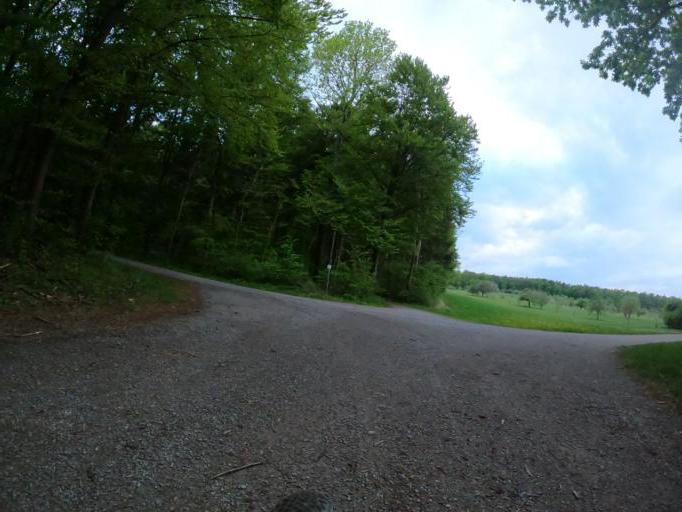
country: DE
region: Baden-Wuerttemberg
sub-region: Regierungsbezirk Stuttgart
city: Aidlingen
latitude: 48.6972
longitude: 8.9138
